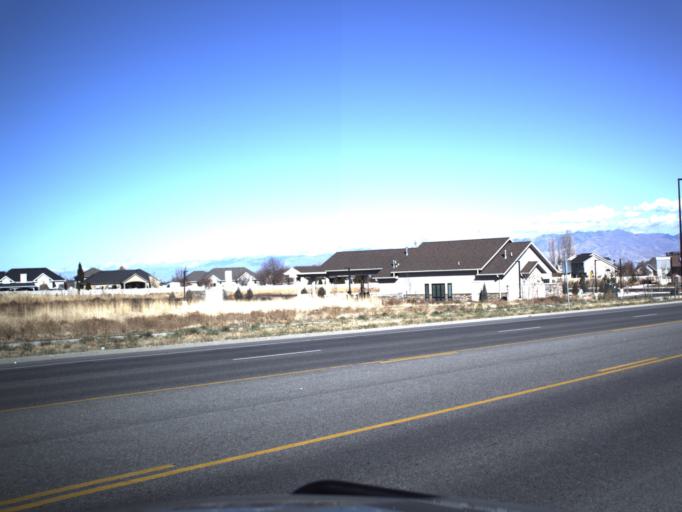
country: US
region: Utah
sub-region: Salt Lake County
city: Oquirrh
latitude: 40.6018
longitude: -112.0068
